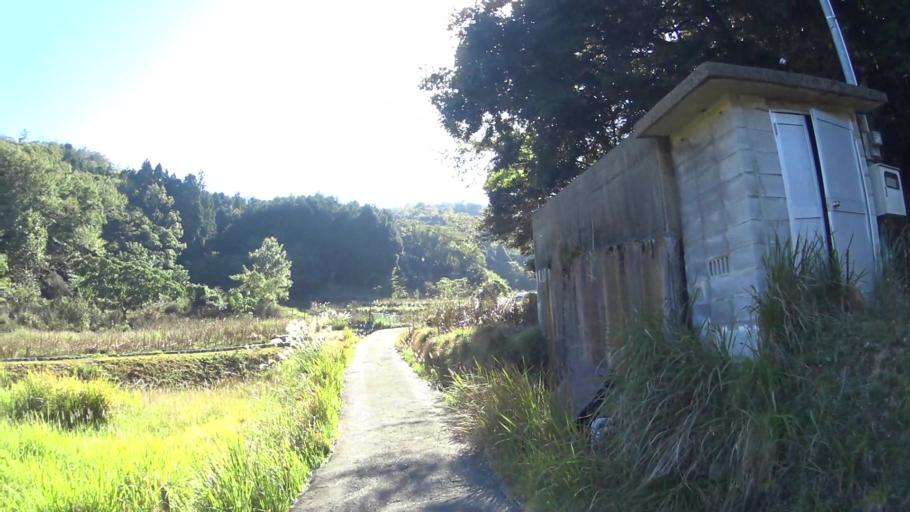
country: JP
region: Hyogo
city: Toyooka
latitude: 35.6472
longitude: 134.8749
